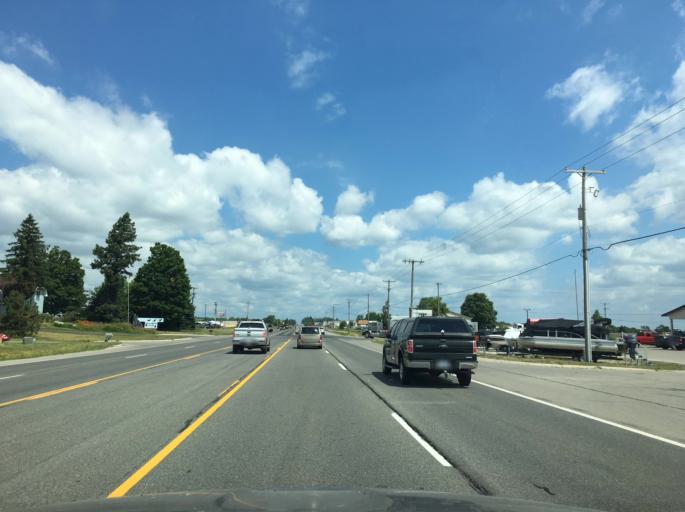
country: US
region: Michigan
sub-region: Grand Traverse County
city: Traverse City
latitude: 44.6888
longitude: -85.6562
